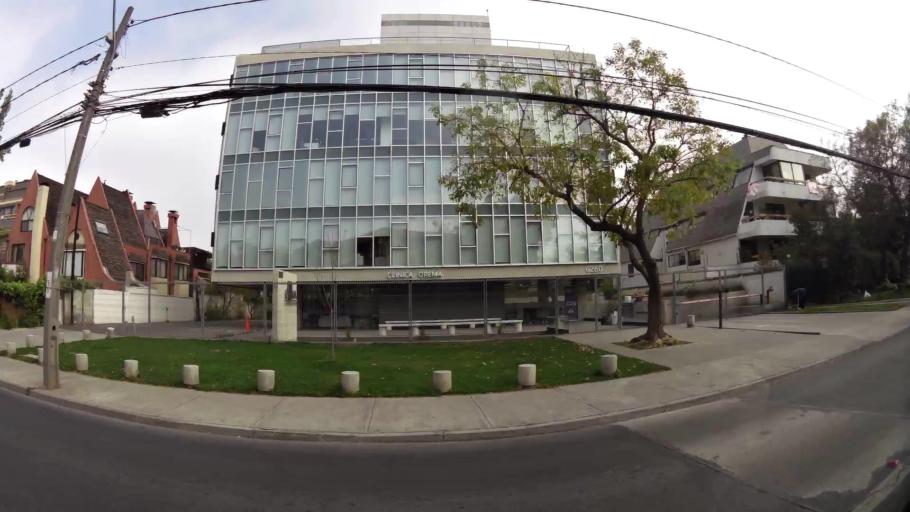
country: CL
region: Santiago Metropolitan
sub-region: Provincia de Santiago
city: Villa Presidente Frei, Nunoa, Santiago, Chile
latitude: -33.3883
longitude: -70.5716
